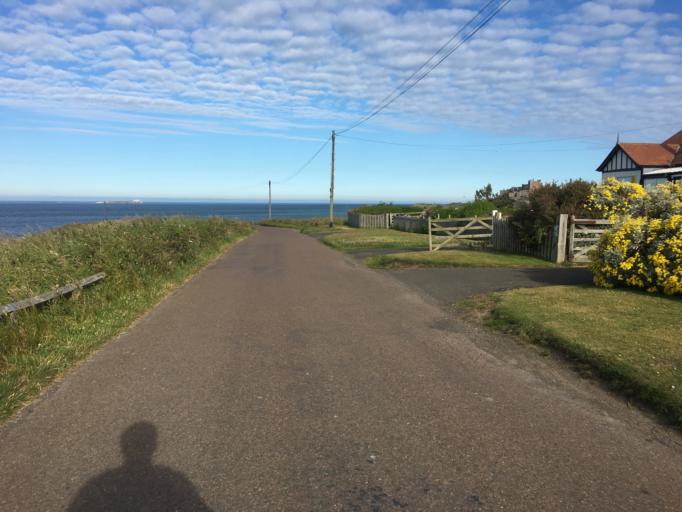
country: GB
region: England
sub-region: Northumberland
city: Bamburgh
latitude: 55.6162
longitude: -1.7264
